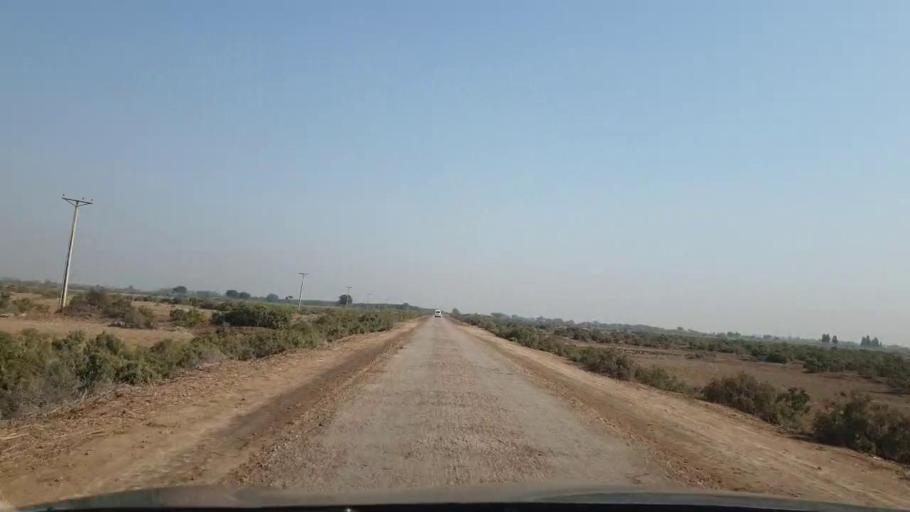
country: PK
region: Sindh
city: Berani
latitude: 25.6248
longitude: 68.8570
